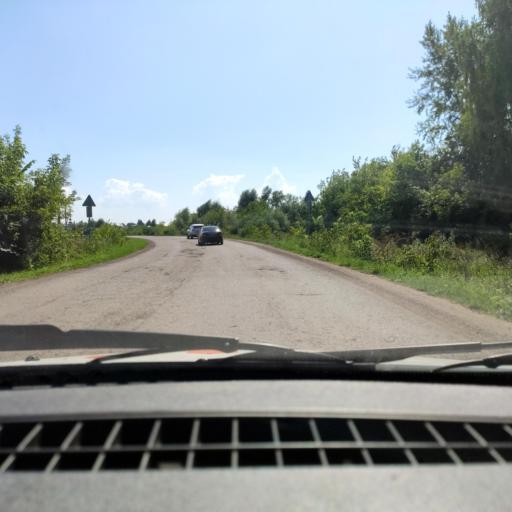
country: RU
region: Bashkortostan
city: Iglino
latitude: 54.8787
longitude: 56.5512
